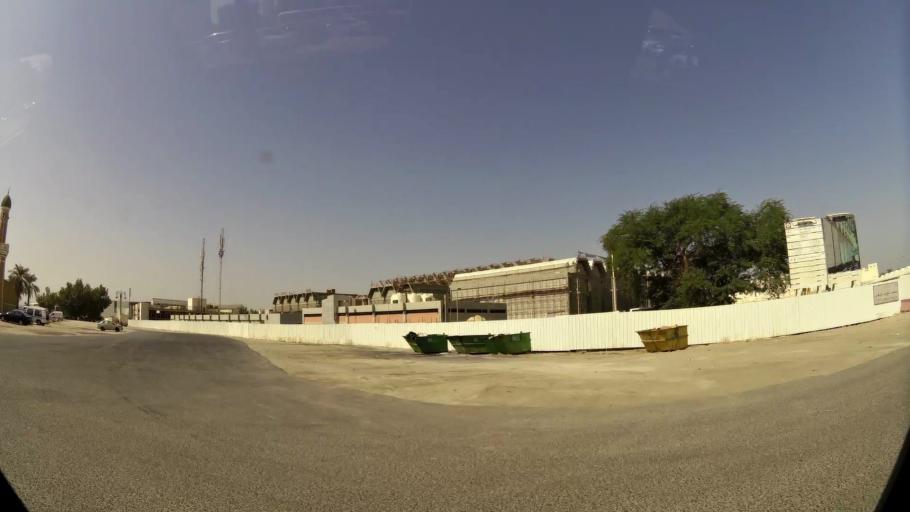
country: KW
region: Al Asimah
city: Kuwait City
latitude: 29.3730
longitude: 47.9686
